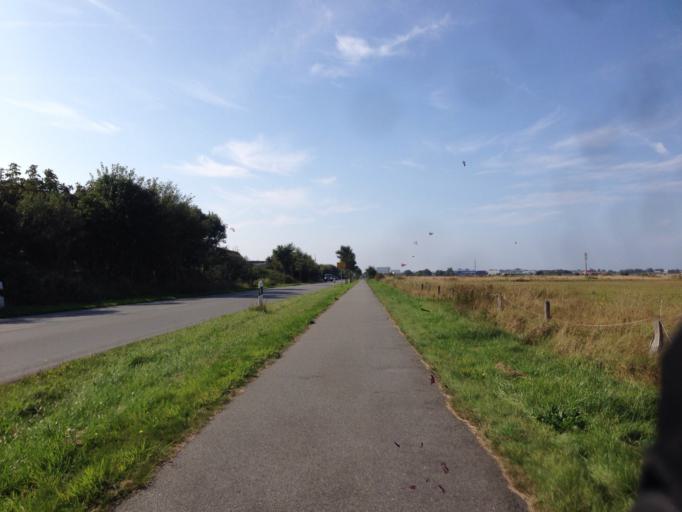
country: DE
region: Schleswig-Holstein
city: Tinnum
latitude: 54.8993
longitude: 8.3472
